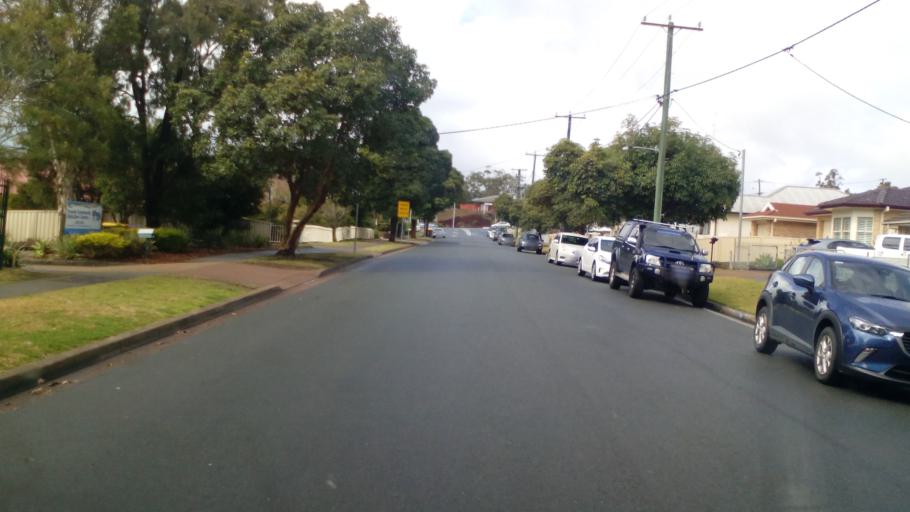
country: AU
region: New South Wales
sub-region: Lake Macquarie Shire
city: Toronto
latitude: -33.0119
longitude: 151.5912
